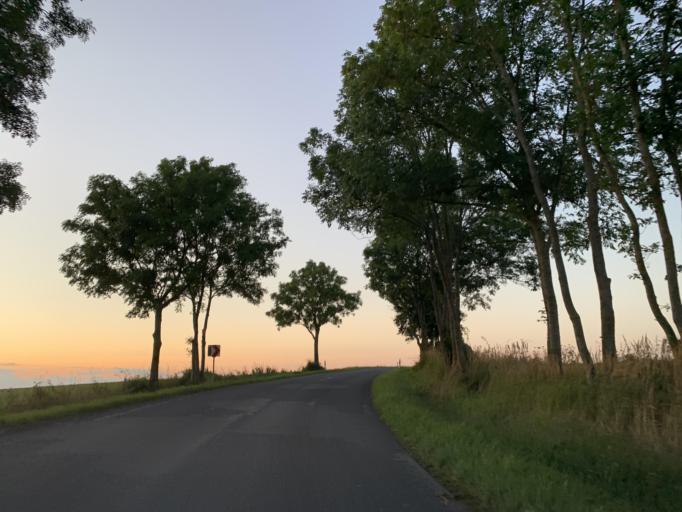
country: DE
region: Mecklenburg-Vorpommern
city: Blankensee
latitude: 53.4488
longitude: 13.2870
